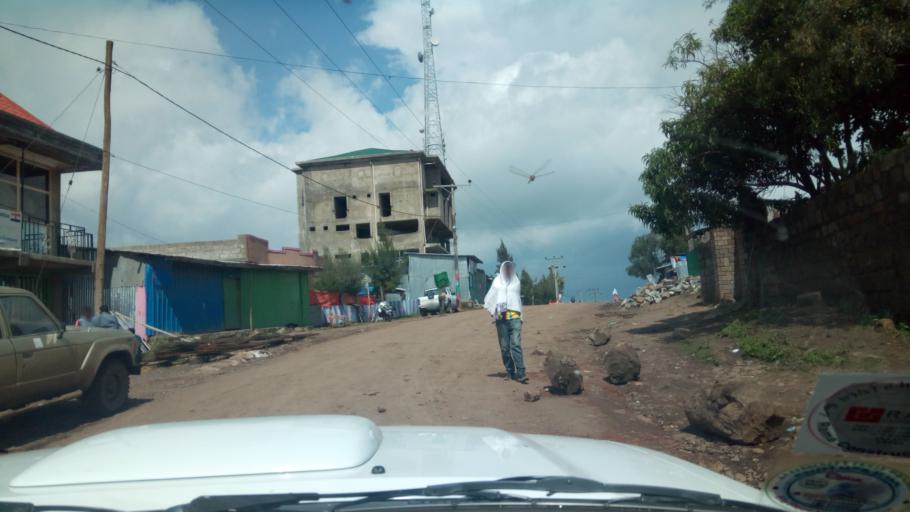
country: ET
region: Oromiya
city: Sendafa
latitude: 8.9707
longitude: 39.1227
